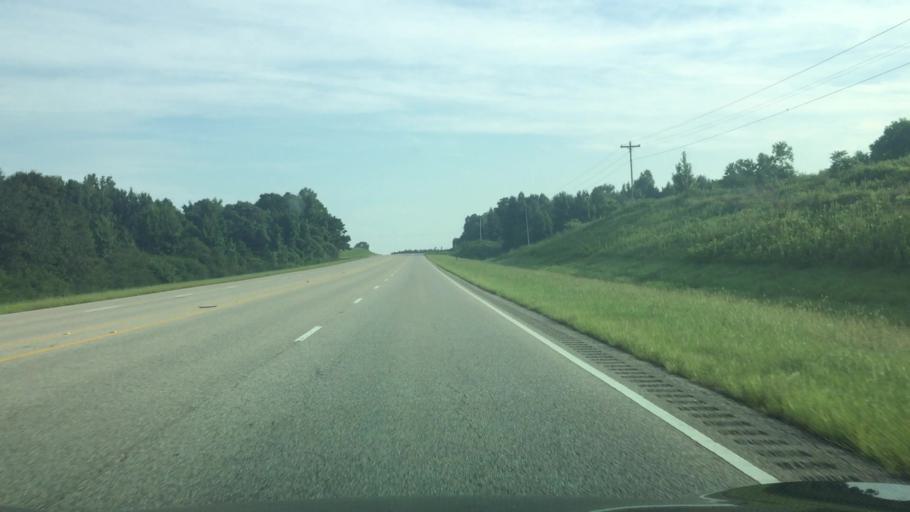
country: US
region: Alabama
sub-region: Covington County
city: Andalusia
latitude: 31.4311
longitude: -86.6116
